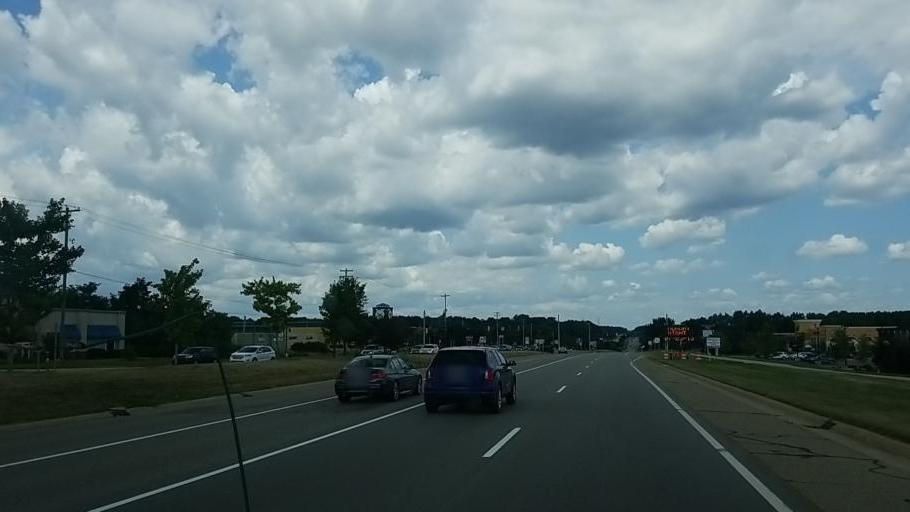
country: US
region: Michigan
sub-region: Kent County
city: Northview
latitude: 42.9995
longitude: -85.5901
